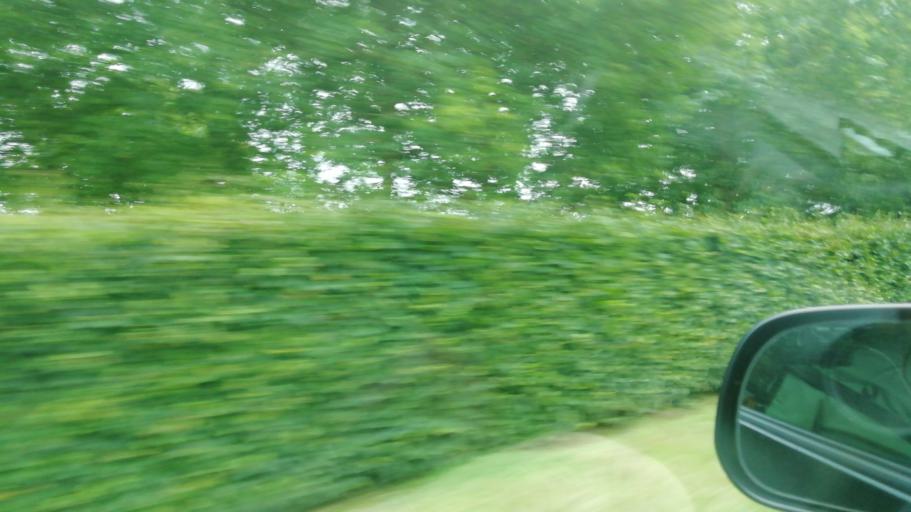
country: IE
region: Munster
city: Fethard
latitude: 52.4981
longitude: -7.6879
